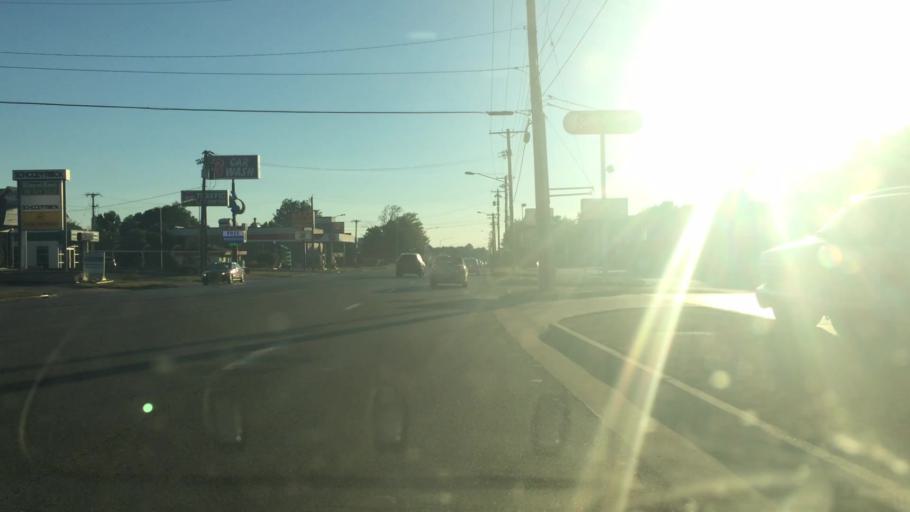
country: US
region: Missouri
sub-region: Greene County
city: Springfield
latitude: 37.1818
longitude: -93.2642
